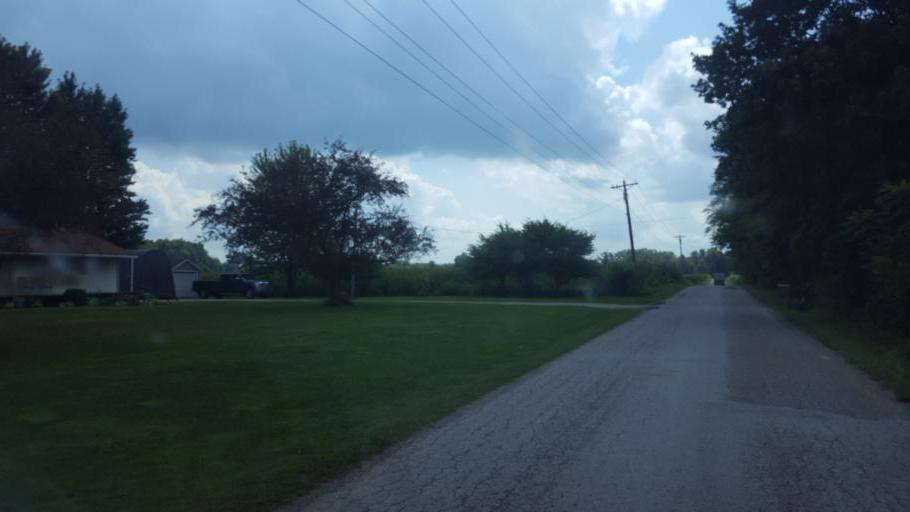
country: US
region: Ohio
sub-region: Knox County
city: Centerburg
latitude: 40.3808
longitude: -82.6537
